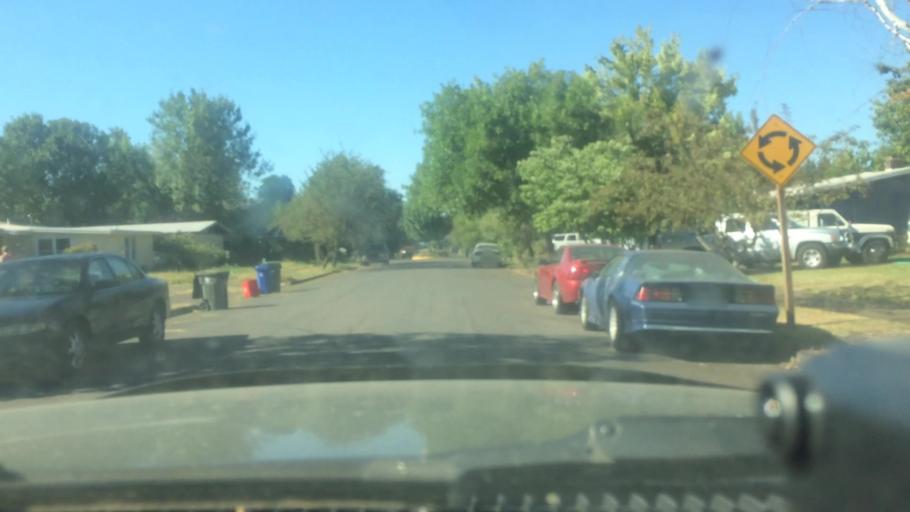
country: US
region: Oregon
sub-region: Lane County
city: Eugene
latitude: 44.0306
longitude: -123.1085
